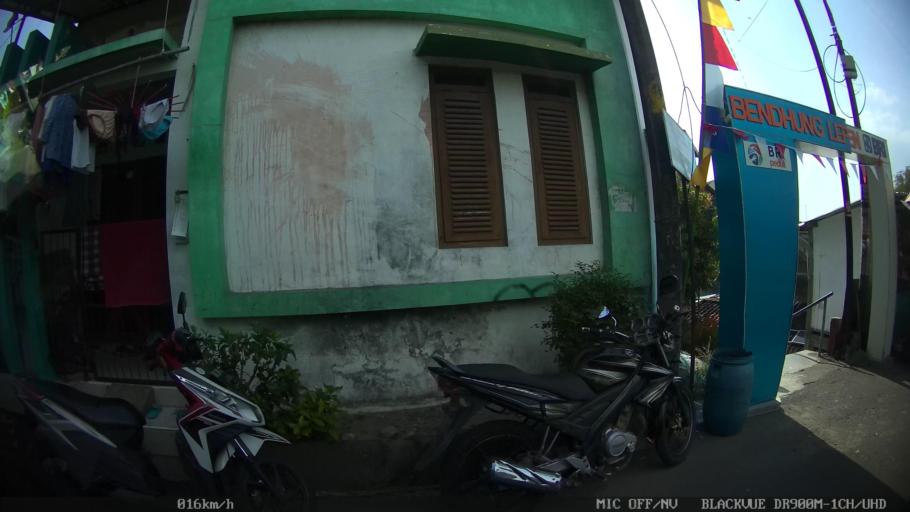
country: ID
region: Daerah Istimewa Yogyakarta
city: Sewon
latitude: -7.8325
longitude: 110.3950
